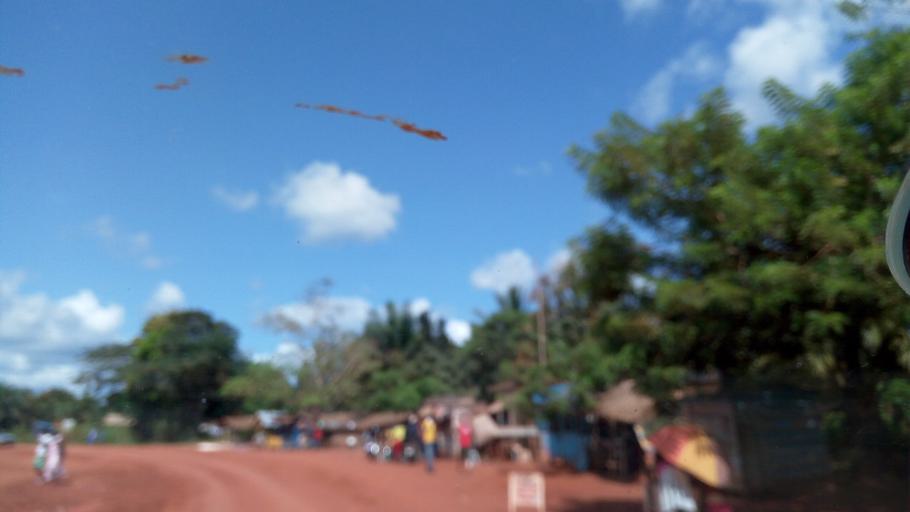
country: CD
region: Equateur
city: Gemena
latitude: 3.2319
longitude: 19.7812
